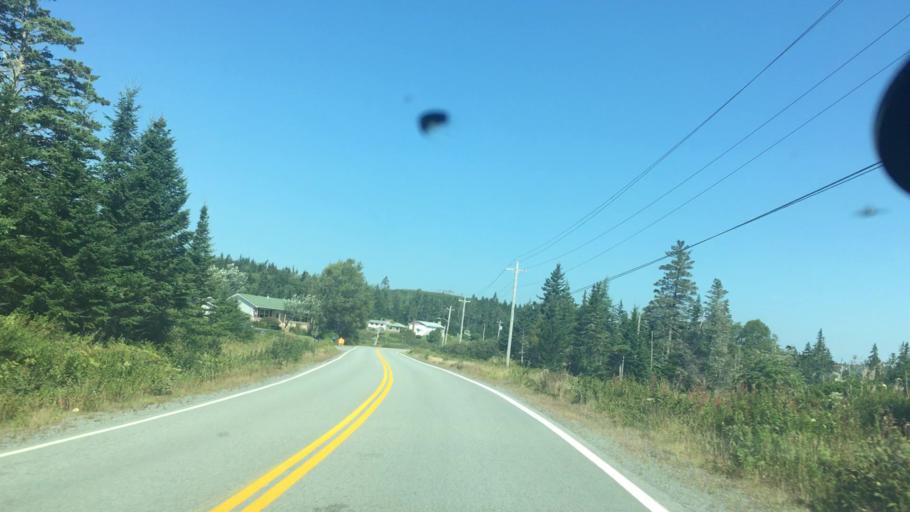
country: CA
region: Nova Scotia
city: New Glasgow
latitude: 44.9253
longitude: -62.2981
